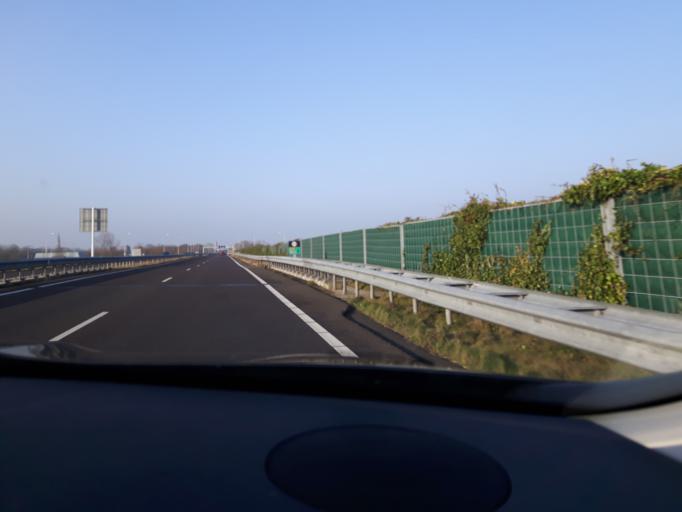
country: NL
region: Zeeland
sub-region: Gemeente Middelburg
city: Middelburg
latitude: 51.4897
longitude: 3.6425
